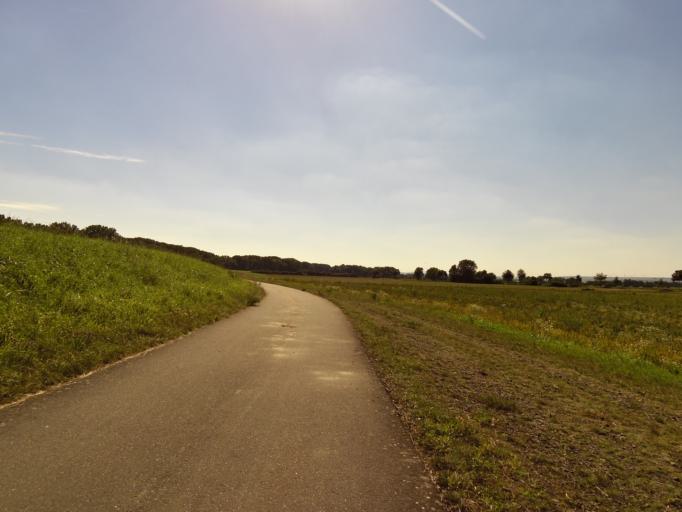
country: DE
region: Rheinland-Pfalz
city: Eich
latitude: 49.7159
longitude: 8.3937
